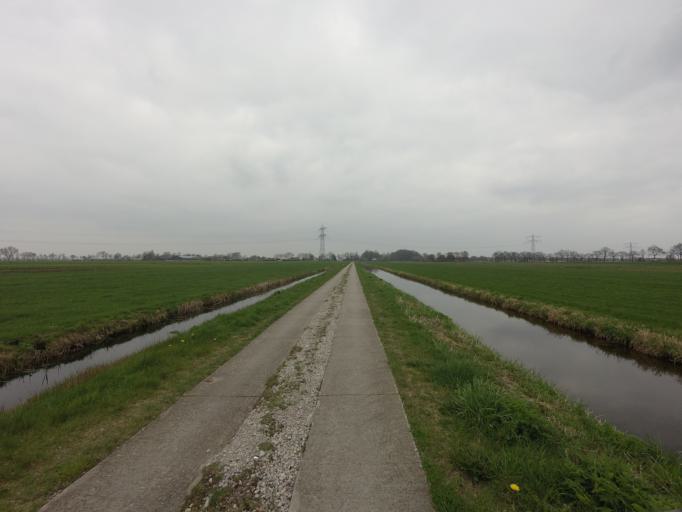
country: NL
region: Utrecht
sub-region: Gemeente De Bilt
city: De Bilt
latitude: 52.1441
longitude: 5.1536
